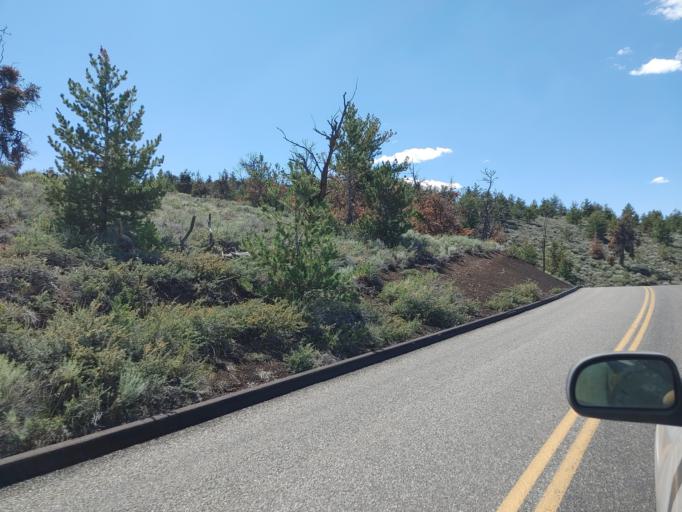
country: US
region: Idaho
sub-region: Butte County
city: Arco
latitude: 43.4533
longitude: -113.5556
